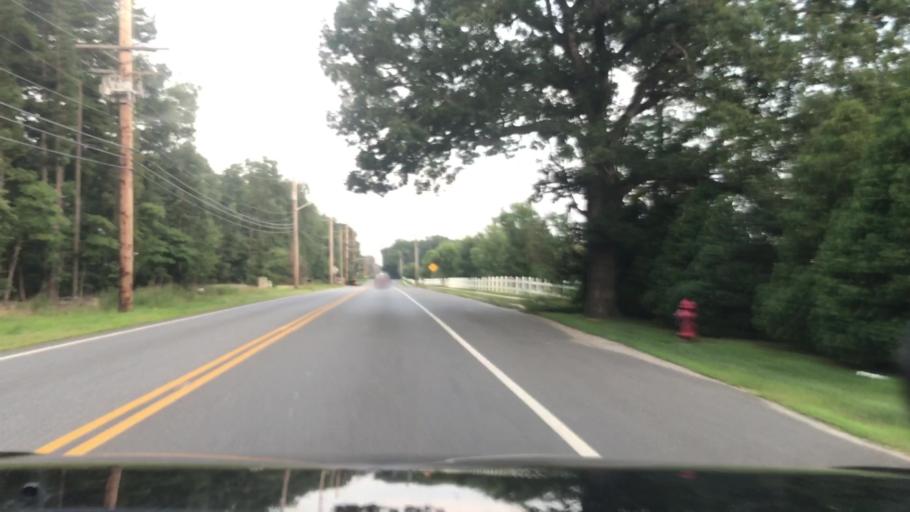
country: US
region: New Jersey
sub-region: Ocean County
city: Lakewood
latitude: 40.0663
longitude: -74.2380
